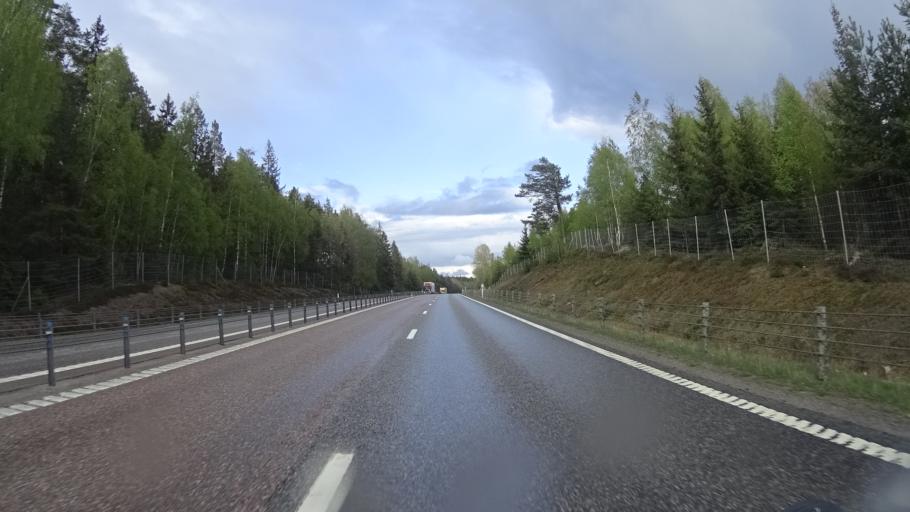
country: SE
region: Vaestmanland
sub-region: Hallstahammars Kommun
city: Hallstahammar
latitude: 59.5810
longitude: 16.1549
